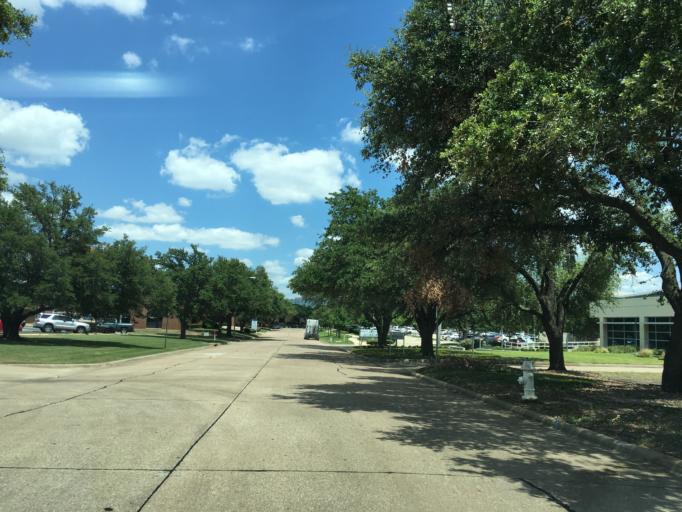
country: US
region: Texas
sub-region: Dallas County
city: Addison
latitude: 32.9503
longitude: -96.8349
